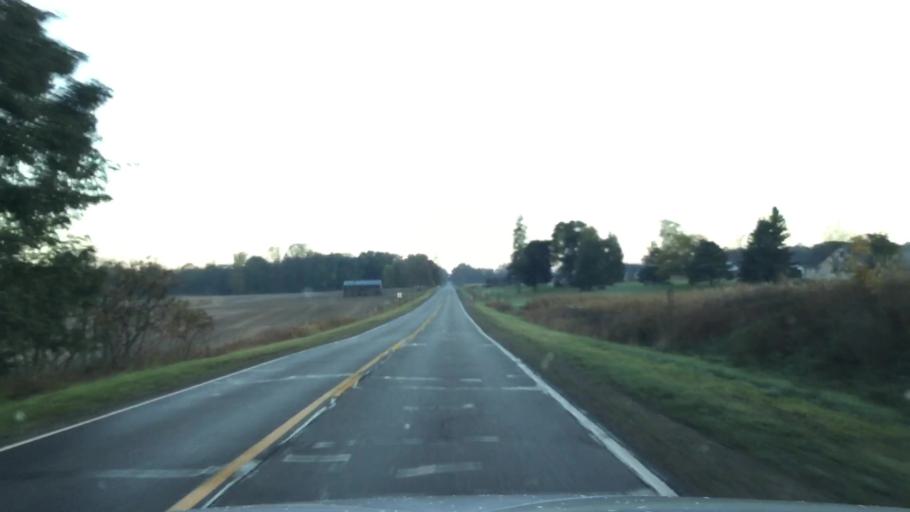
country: US
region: Michigan
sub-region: Livingston County
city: Howell
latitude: 42.6714
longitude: -83.9361
